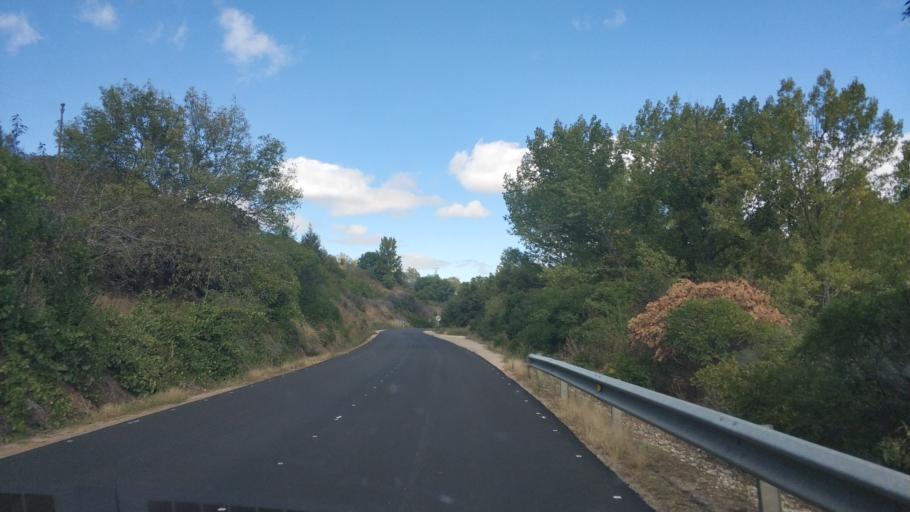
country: ES
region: Castille and Leon
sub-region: Provincia de Burgos
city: Covarrubias
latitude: 42.0551
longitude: -3.5241
